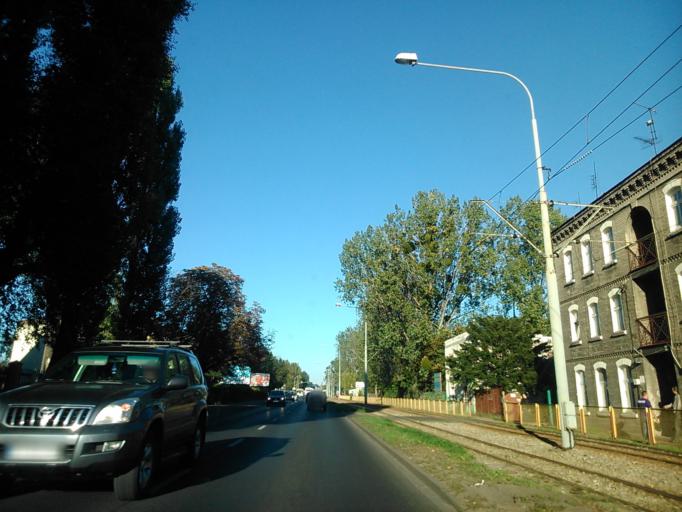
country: PL
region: Kujawsko-Pomorskie
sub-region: Torun
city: Torun
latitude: 53.0279
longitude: 18.6388
